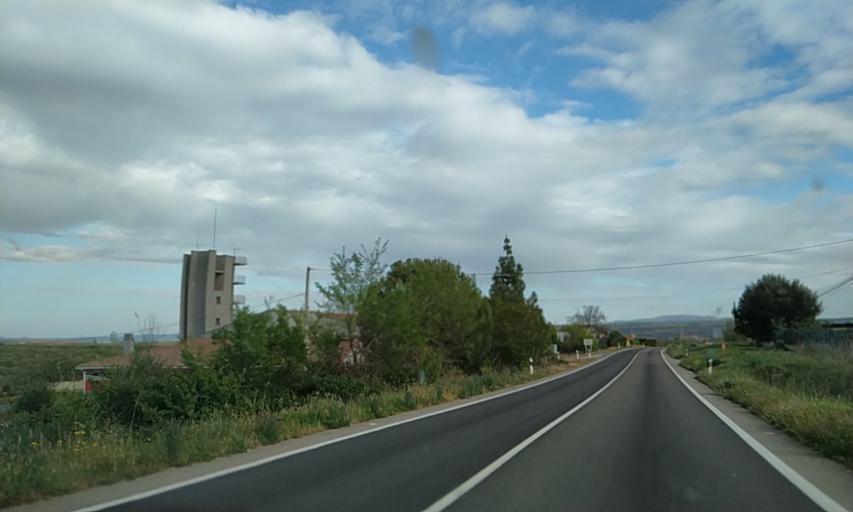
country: ES
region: Extremadura
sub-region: Provincia de Caceres
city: Coria
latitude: 40.0035
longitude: -6.5524
